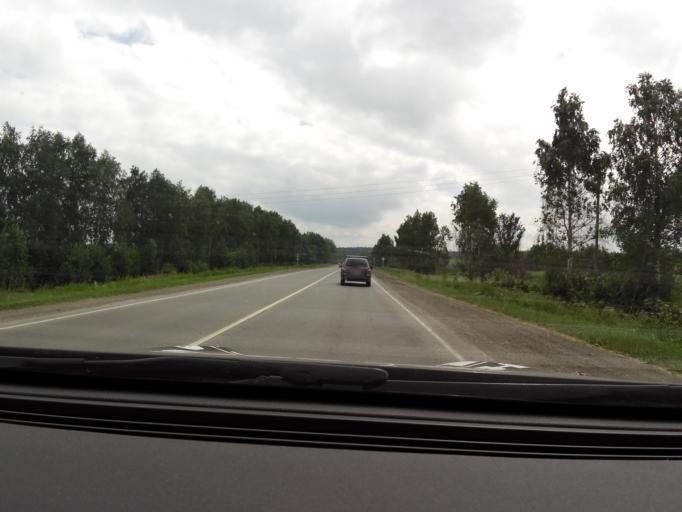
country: RU
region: Perm
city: Kukushtan
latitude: 57.4961
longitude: 56.6594
